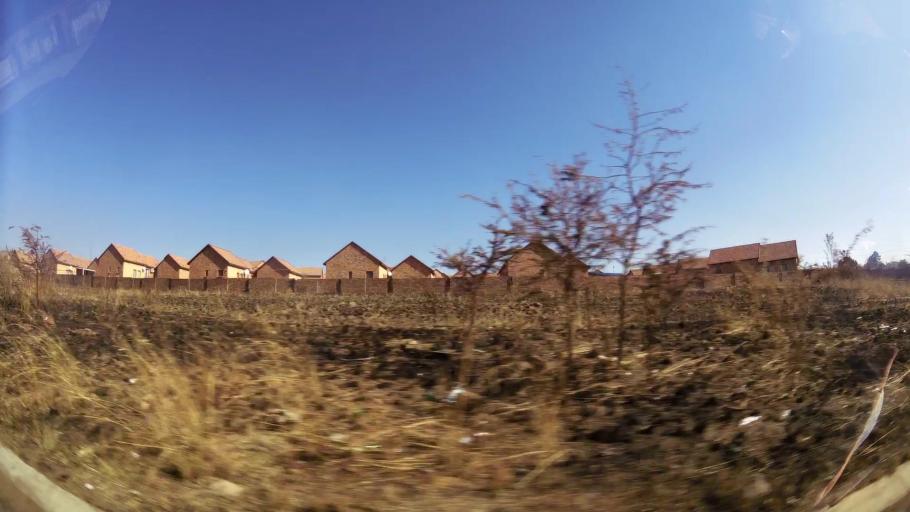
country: ZA
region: Mpumalanga
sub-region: Nkangala District Municipality
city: Witbank
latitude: -25.8657
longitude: 29.2568
